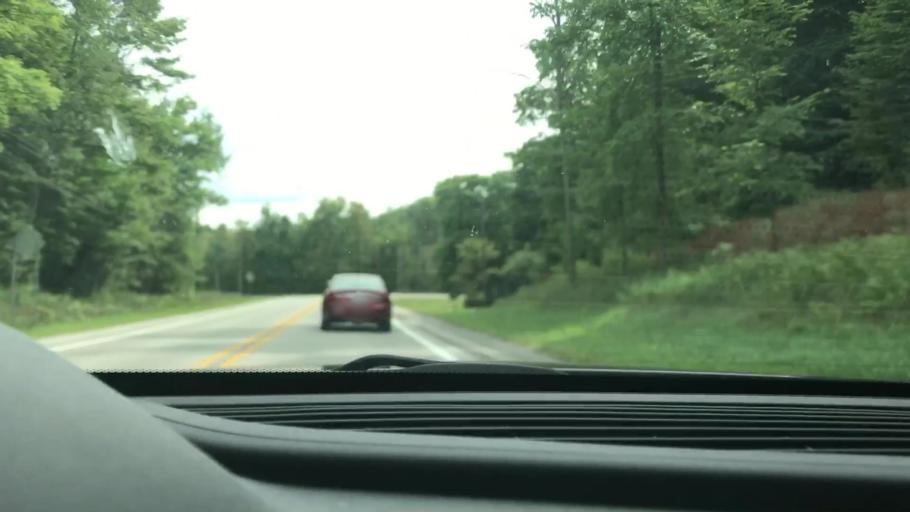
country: US
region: Michigan
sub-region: Antrim County
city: Bellaire
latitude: 45.0803
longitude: -85.2835
